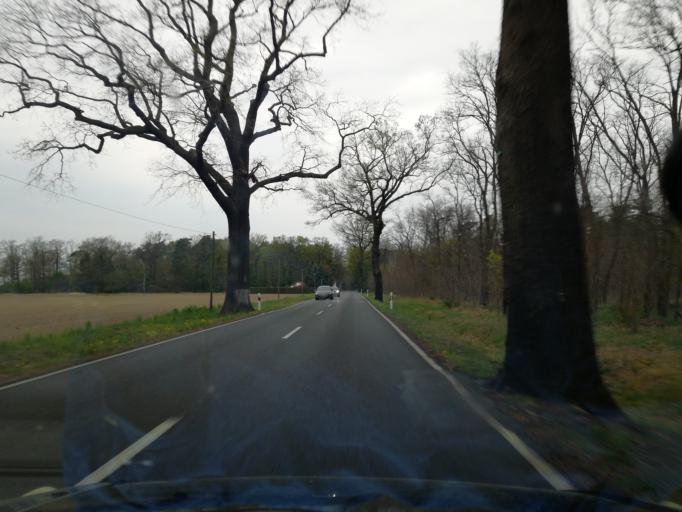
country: DE
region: Brandenburg
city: Calau
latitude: 51.7686
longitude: 13.9020
